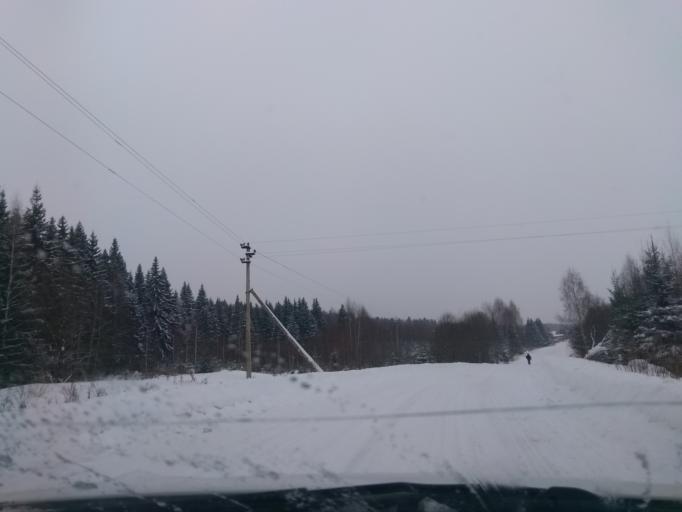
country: RU
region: Perm
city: Sylva
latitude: 57.8412
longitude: 56.7430
